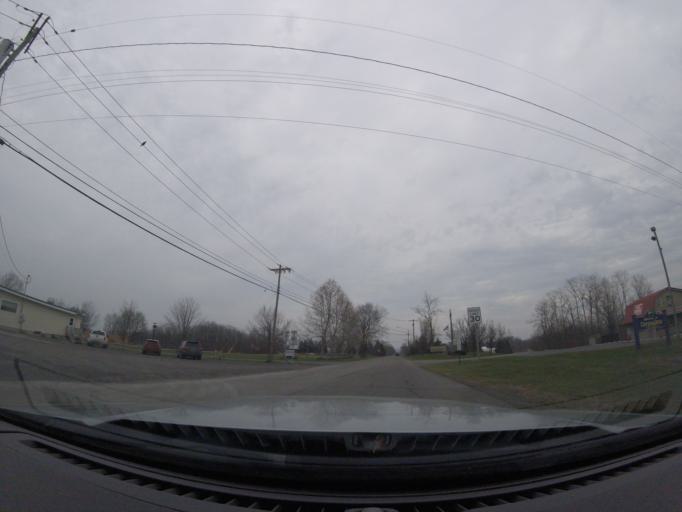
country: US
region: New York
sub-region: Yates County
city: Penn Yan
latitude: 42.6808
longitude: -76.9628
